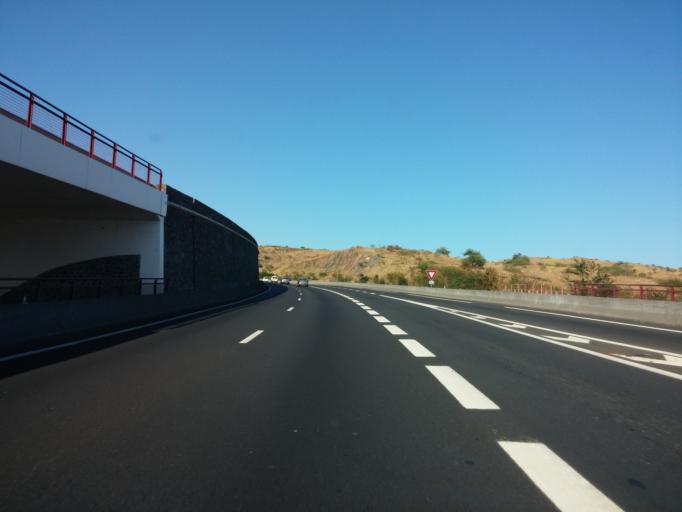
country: RE
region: Reunion
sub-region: Reunion
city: Saint-Paul
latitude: -21.0215
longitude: 55.2563
